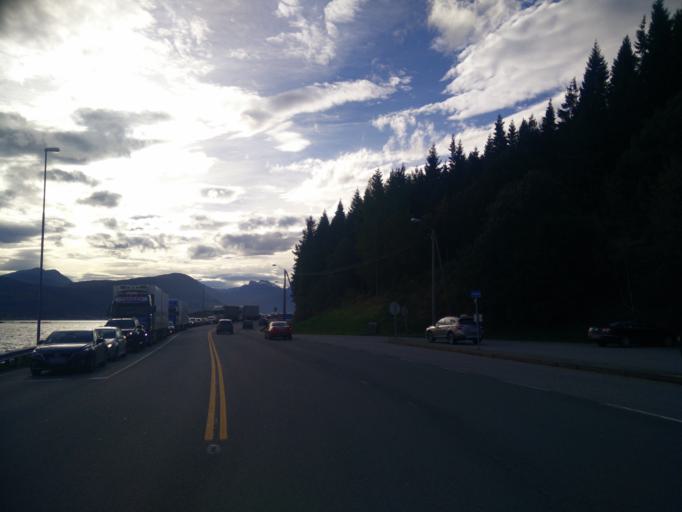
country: NO
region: More og Romsdal
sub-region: Vestnes
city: Vestnes
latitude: 62.6517
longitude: 7.0851
